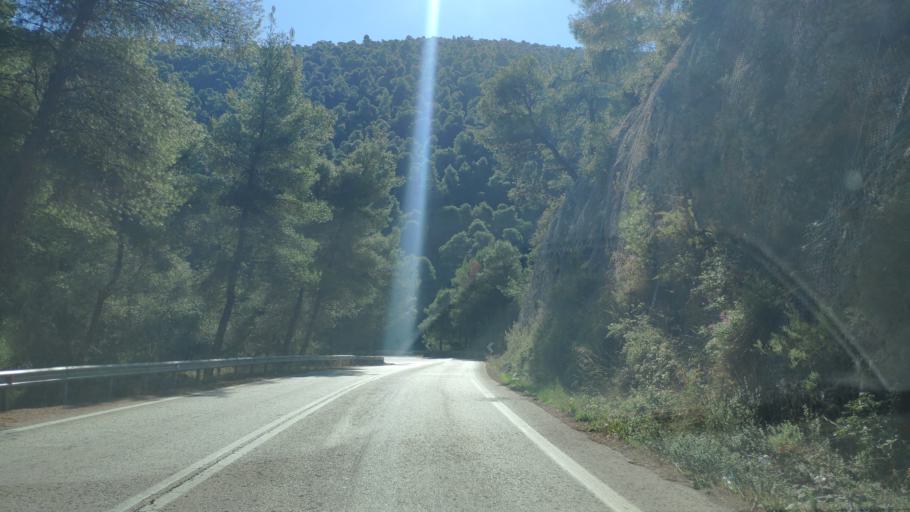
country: GR
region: Peloponnese
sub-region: Nomos Korinthias
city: Sofikon
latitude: 37.8236
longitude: 23.0827
